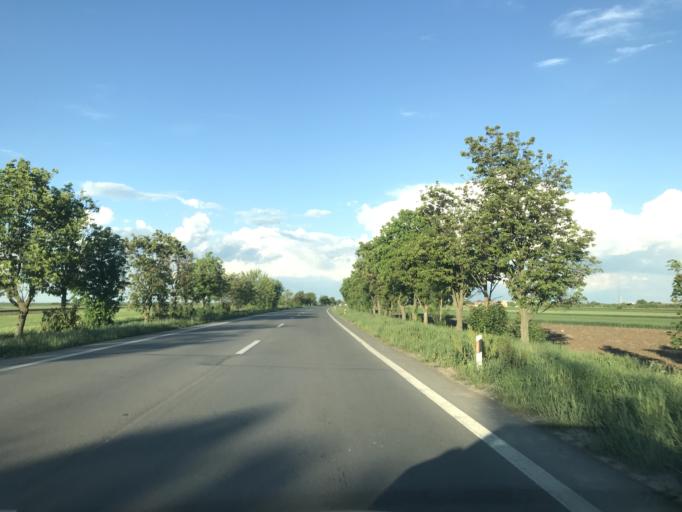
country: RS
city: Aradac
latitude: 45.3920
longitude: 20.2877
